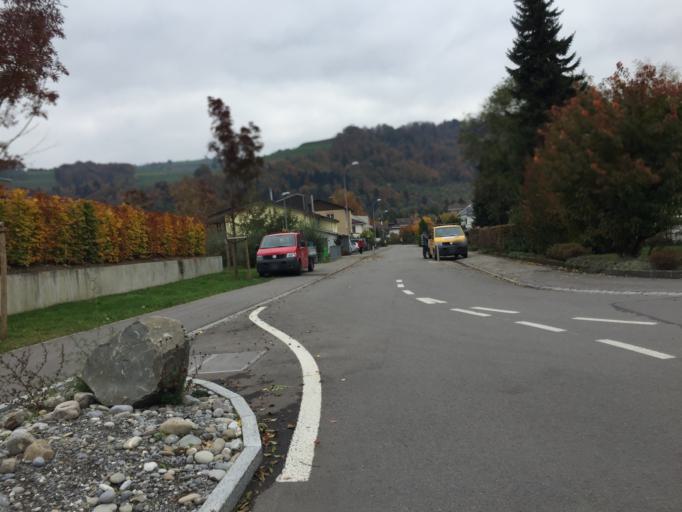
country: CH
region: Bern
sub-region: Bern-Mittelland District
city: Munsingen
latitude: 46.8718
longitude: 7.5521
